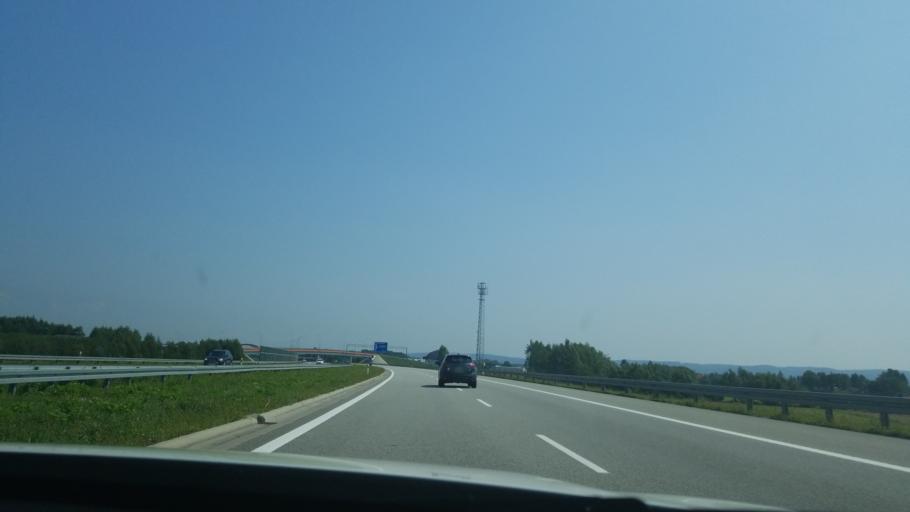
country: PL
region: Subcarpathian Voivodeship
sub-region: Powiat debicki
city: Zyrakow
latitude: 50.0792
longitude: 21.3698
